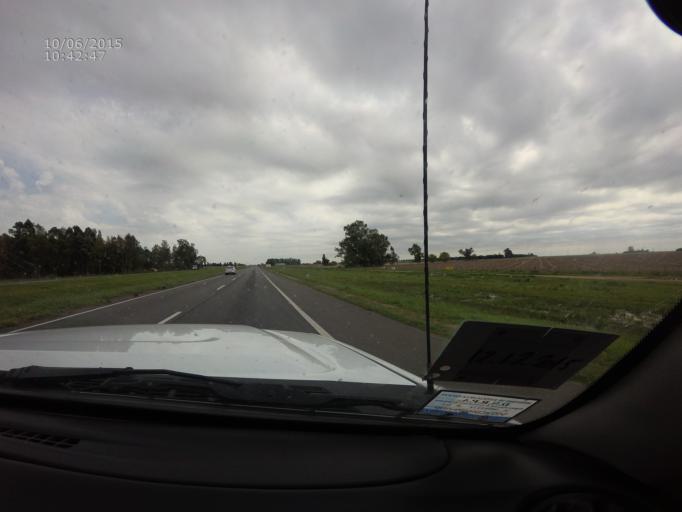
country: AR
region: Buenos Aires
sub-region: Partido de Ramallo
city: Ramallo
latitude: -33.4736
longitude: -60.1549
